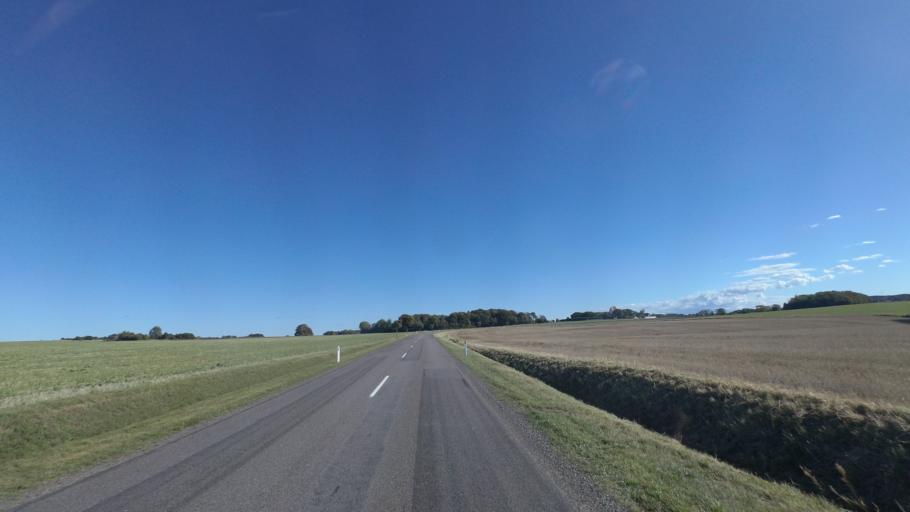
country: DK
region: Capital Region
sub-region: Bornholm Kommune
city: Nexo
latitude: 55.1219
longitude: 15.0977
